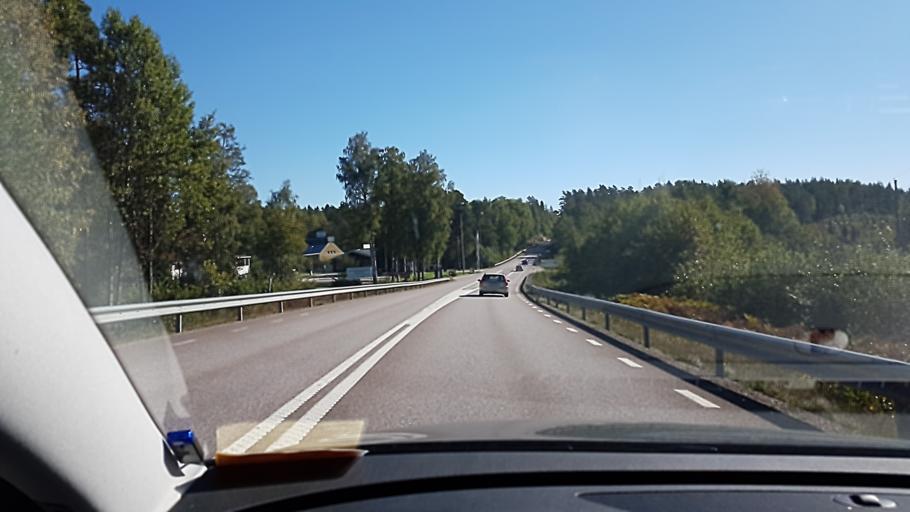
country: SE
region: Kronoberg
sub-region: Lessebo Kommun
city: Lessebo
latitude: 56.7823
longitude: 15.2196
